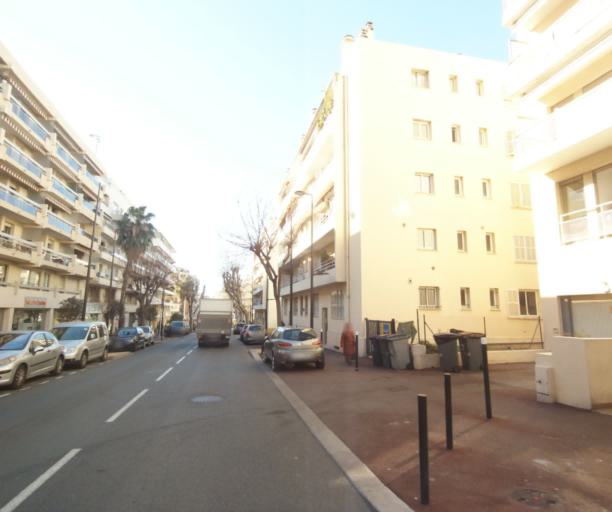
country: FR
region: Provence-Alpes-Cote d'Azur
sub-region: Departement des Alpes-Maritimes
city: Antibes
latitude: 43.5721
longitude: 7.1153
